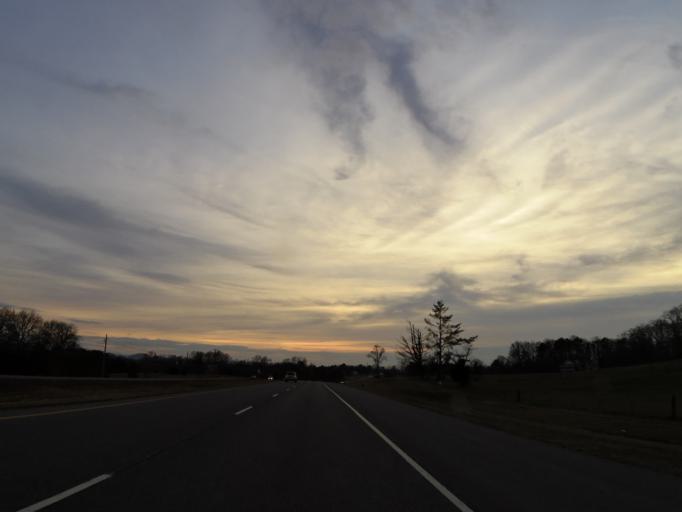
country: US
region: Tennessee
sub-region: McMinn County
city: Englewood
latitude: 35.4663
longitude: -84.4211
